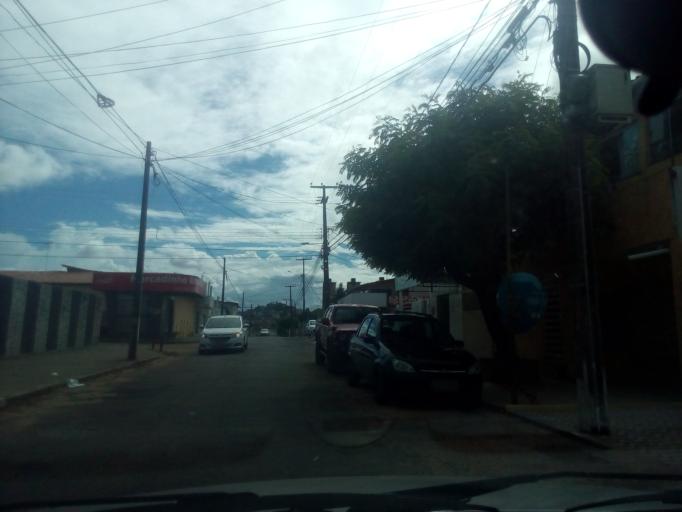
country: BR
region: Rio Grande do Norte
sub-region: Parnamirim
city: Parnamirim
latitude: -5.8702
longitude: -35.2042
